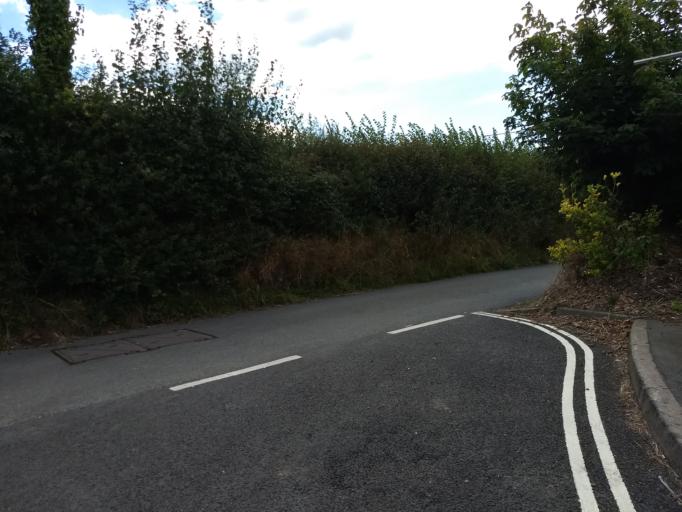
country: GB
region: England
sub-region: Isle of Wight
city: Newchurch
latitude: 50.7103
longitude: -1.2044
